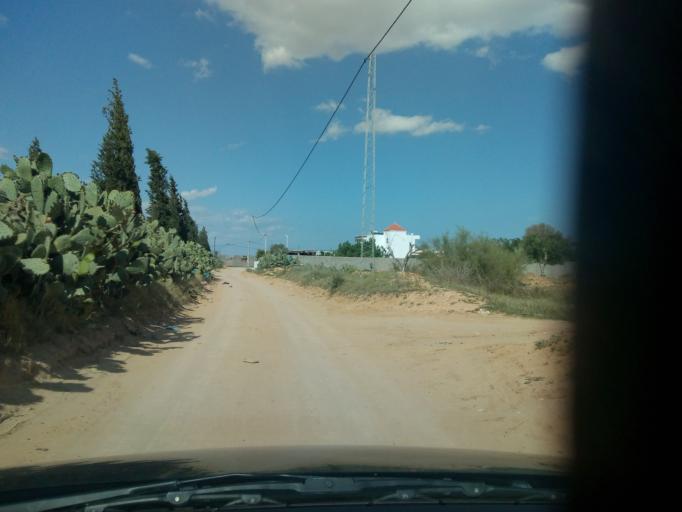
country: TN
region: Safaqis
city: Sfax
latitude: 34.7272
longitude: 10.6101
